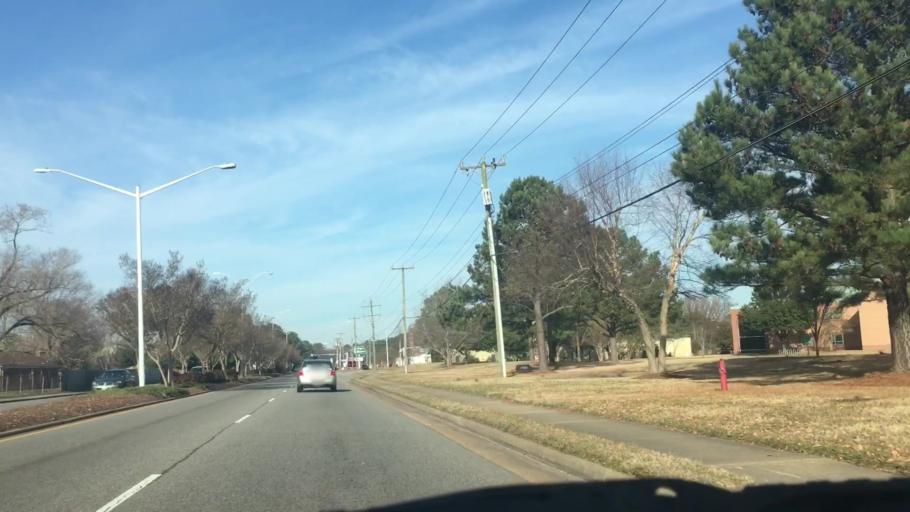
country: US
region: Virginia
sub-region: City of Chesapeake
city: Chesapeake
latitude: 36.8137
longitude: -76.1425
